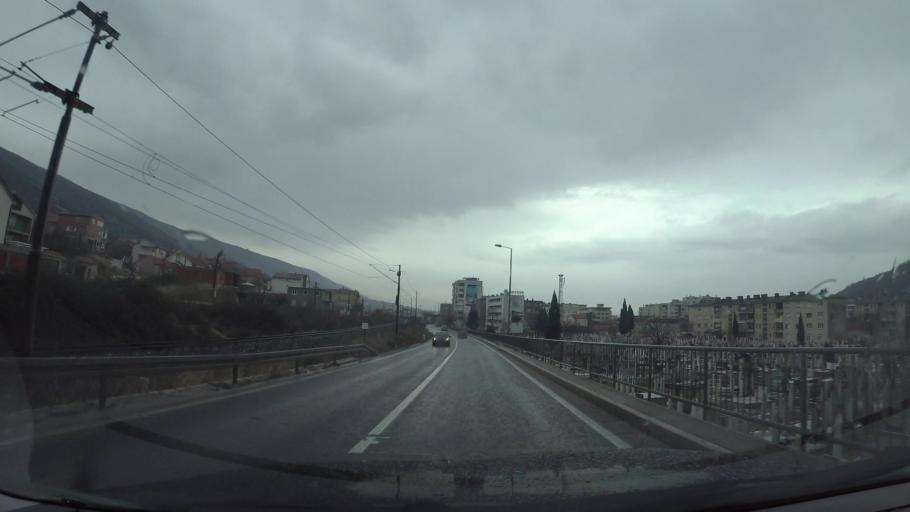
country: BA
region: Federation of Bosnia and Herzegovina
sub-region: Hercegovacko-Bosanski Kanton
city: Mostar
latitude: 43.3300
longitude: 17.8218
